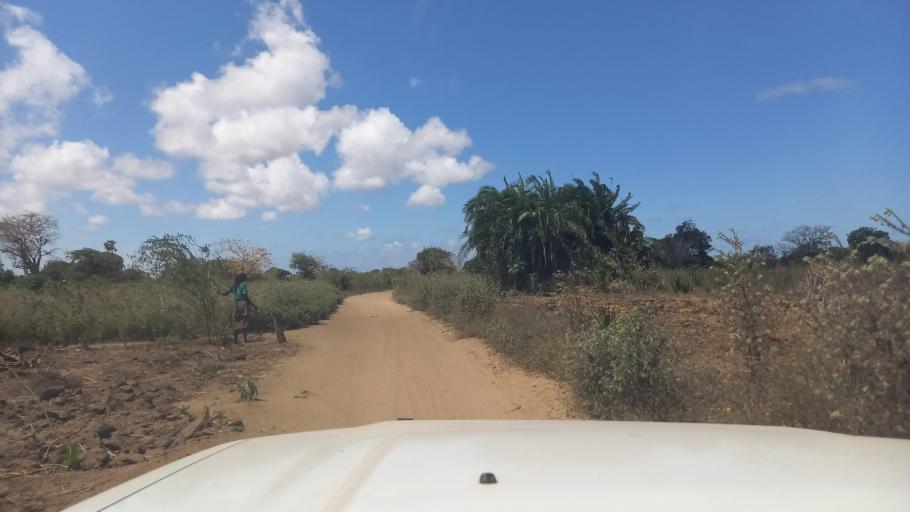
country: MZ
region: Cabo Delgado
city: Pemba
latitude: -13.4240
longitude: 40.5007
